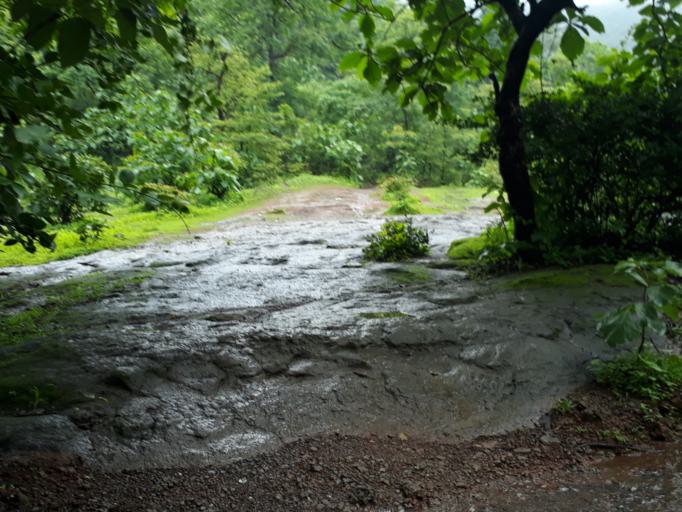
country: IN
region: Maharashtra
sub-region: Raigarh
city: Khopoli
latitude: 18.8438
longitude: 73.3795
